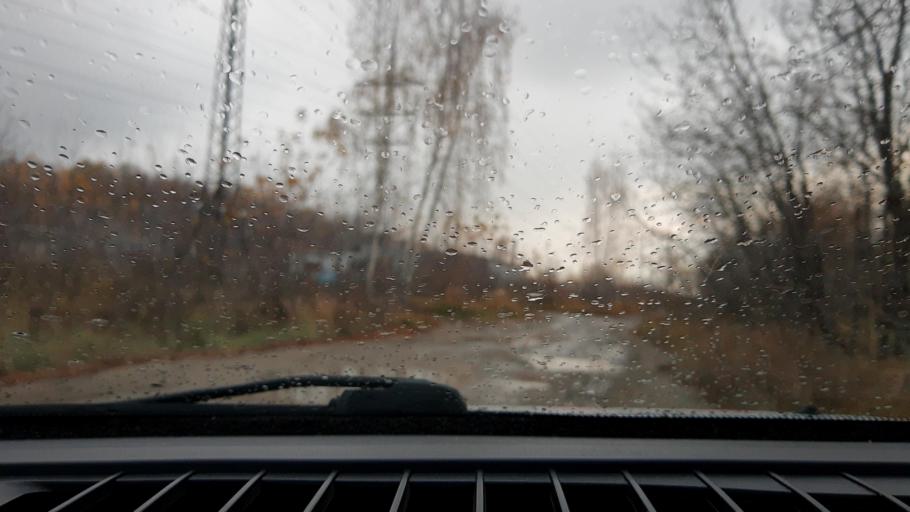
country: RU
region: Nizjnij Novgorod
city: Gorbatovka
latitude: 56.3507
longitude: 43.8328
